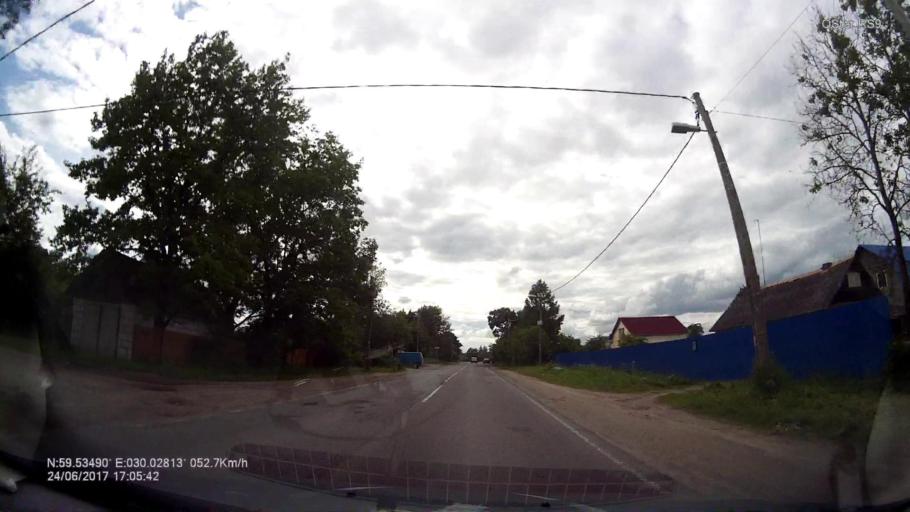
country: RU
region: Leningrad
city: Mariyenburg
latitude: 59.5349
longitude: 30.0278
